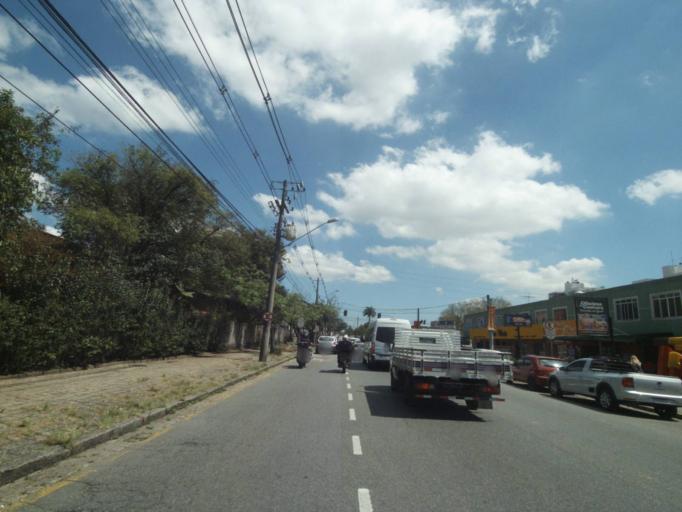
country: BR
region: Parana
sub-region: Curitiba
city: Curitiba
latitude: -25.3991
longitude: -49.2461
